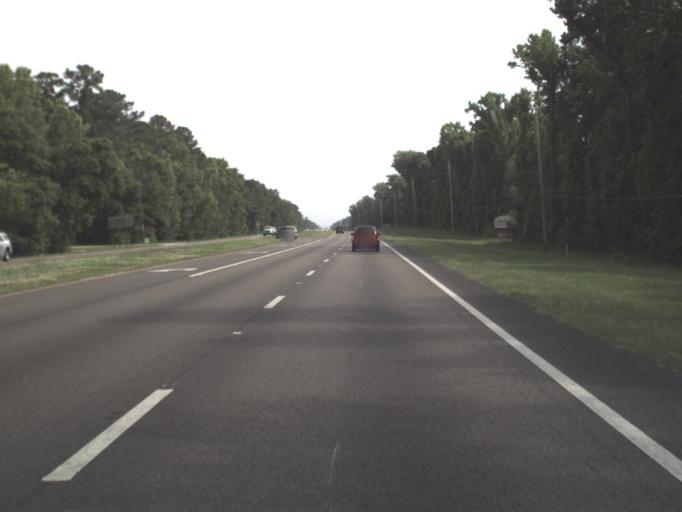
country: US
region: Florida
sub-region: Clay County
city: Green Cove Springs
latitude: 30.0462
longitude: -81.7084
